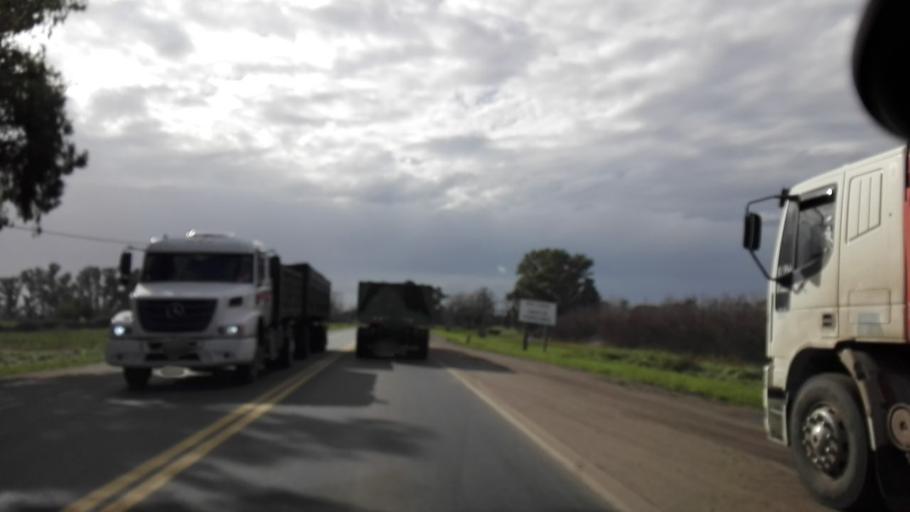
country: AR
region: Buenos Aires
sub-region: Partido de Las Flores
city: Las Flores
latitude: -36.0189
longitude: -59.0736
